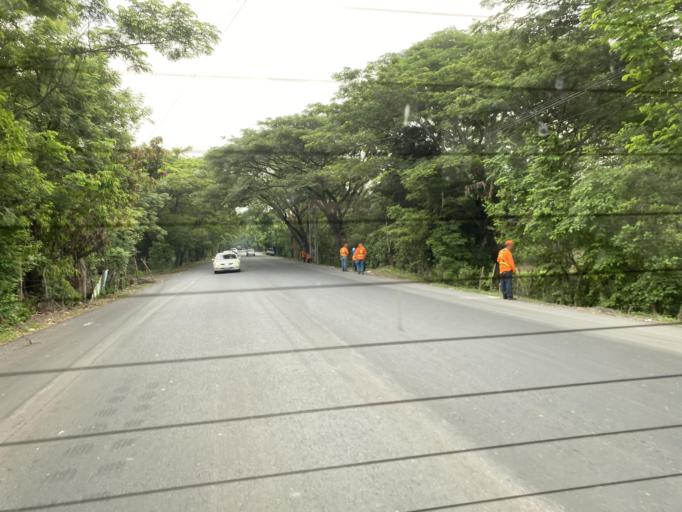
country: SV
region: San Miguel
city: Chirilagua
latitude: 13.3480
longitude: -88.1475
